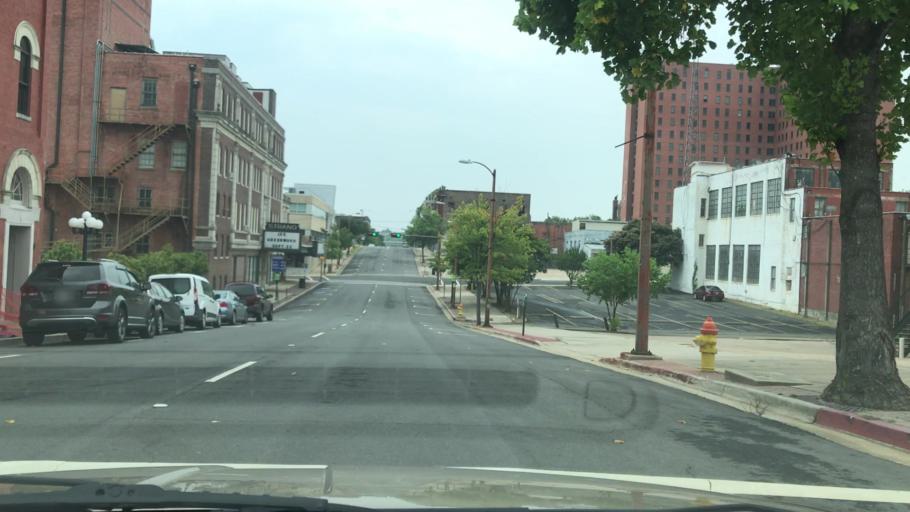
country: US
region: Louisiana
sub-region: Caddo Parish
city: Shreveport
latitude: 32.5106
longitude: -93.7508
